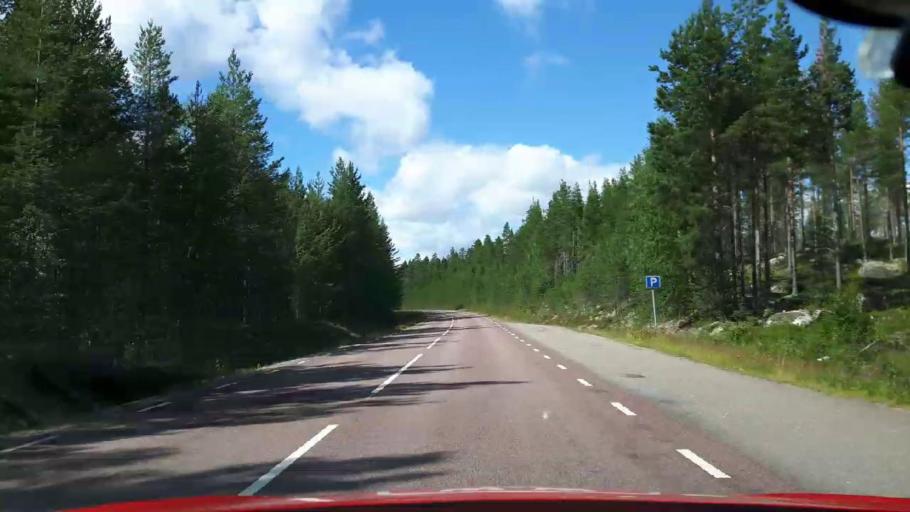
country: SE
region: Jaemtland
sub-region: Harjedalens Kommun
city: Sveg
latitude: 62.0013
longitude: 14.2729
